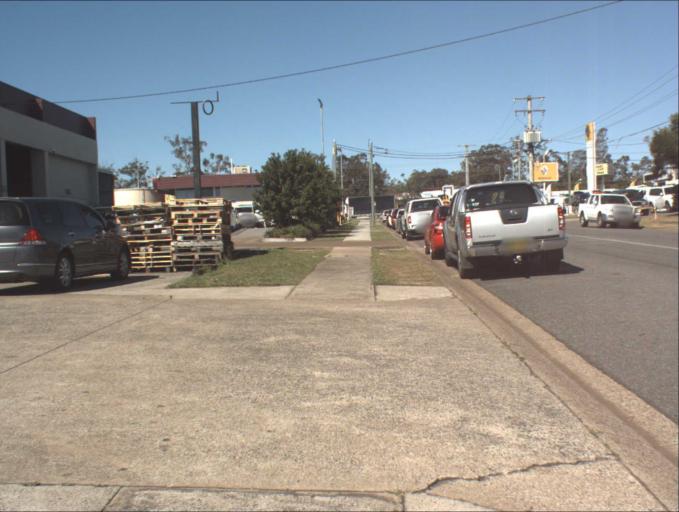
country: AU
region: Queensland
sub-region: Logan
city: Springwood
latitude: -27.6304
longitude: 153.1292
